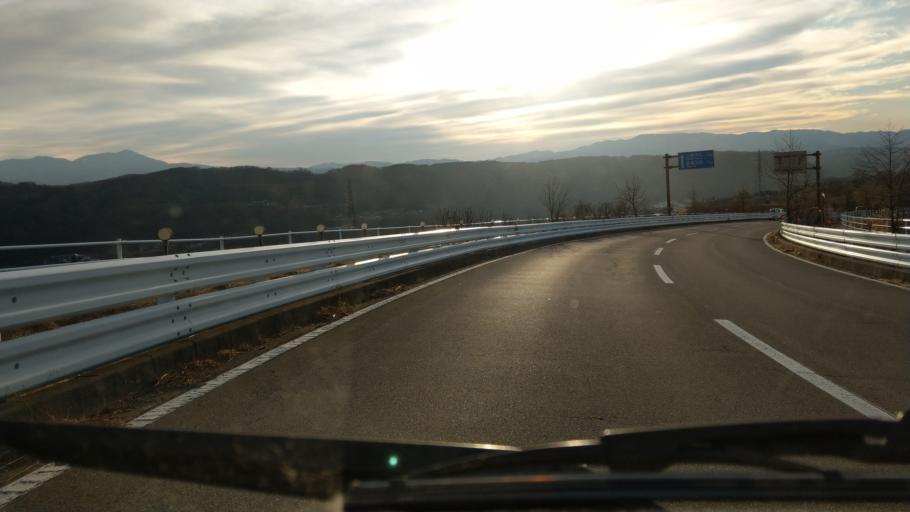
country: JP
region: Nagano
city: Komoro
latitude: 36.3437
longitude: 138.4110
